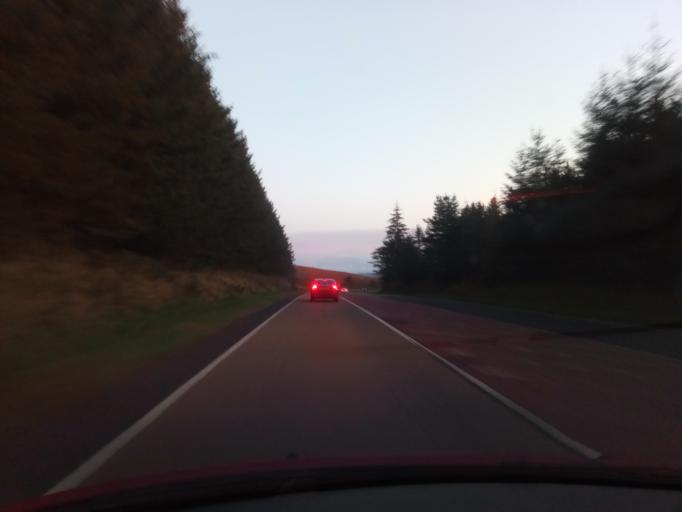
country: GB
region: Scotland
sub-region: East Lothian
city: Pencaitland
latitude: 55.8068
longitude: -2.8365
